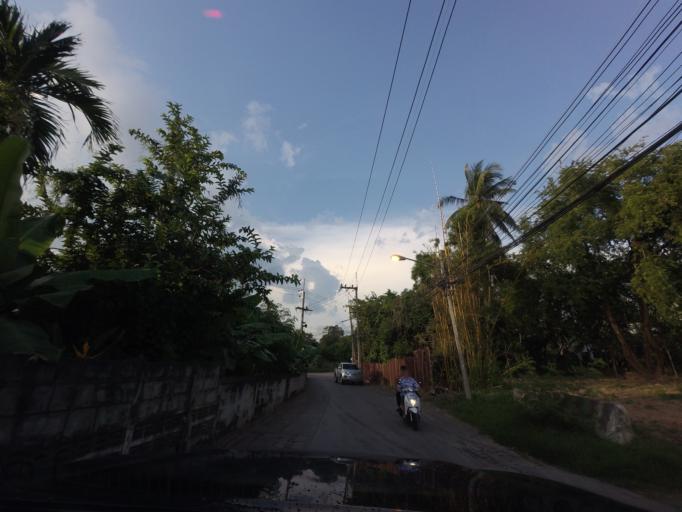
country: TH
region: Khon Kaen
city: Khon Kaen
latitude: 16.4262
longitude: 102.8605
